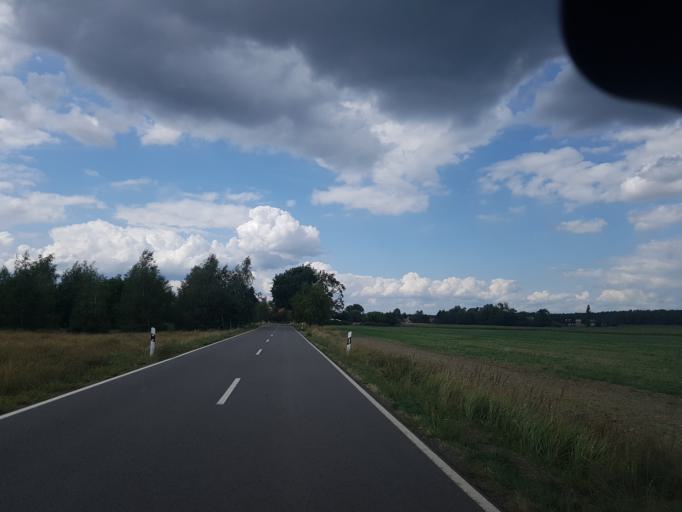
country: DE
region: Brandenburg
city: Schlieben
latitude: 51.6900
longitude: 13.3352
